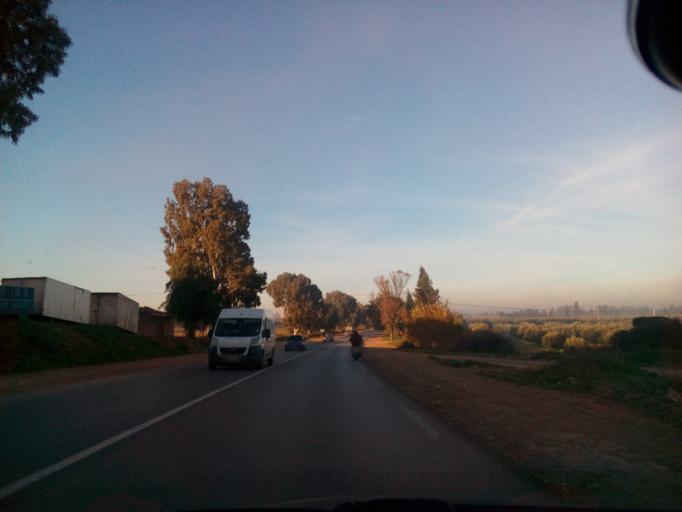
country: DZ
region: Relizane
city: Relizane
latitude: 35.7262
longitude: 0.3946
